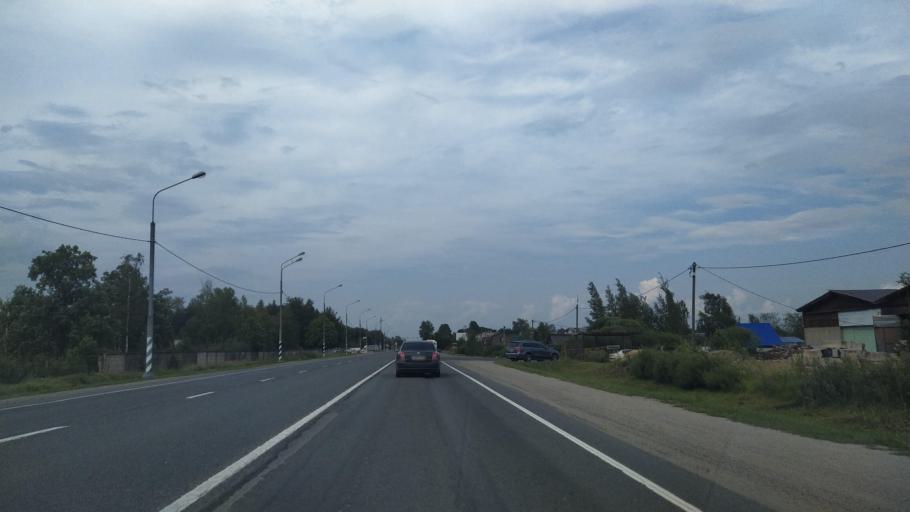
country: RU
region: Novgorod
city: Pankovka
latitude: 58.4872
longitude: 31.1964
